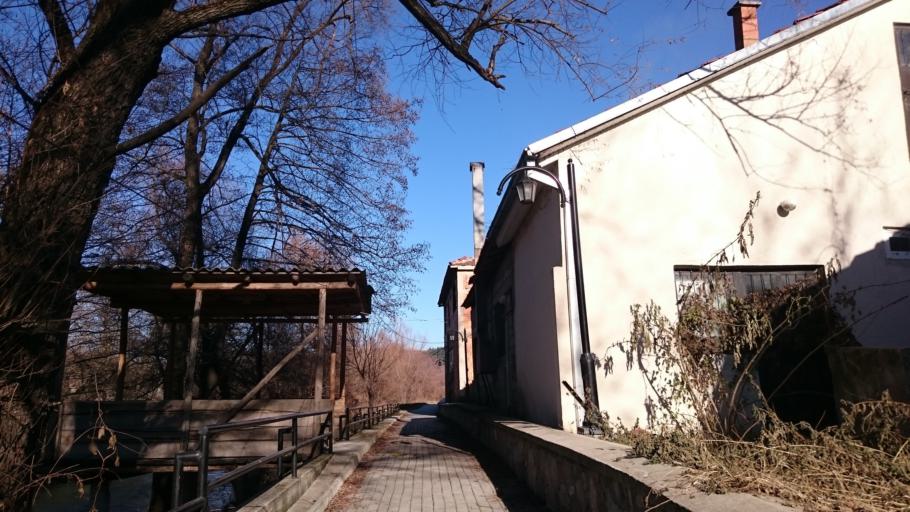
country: MK
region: Makedonski Brod
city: Makedonski Brod
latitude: 41.5082
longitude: 21.2170
